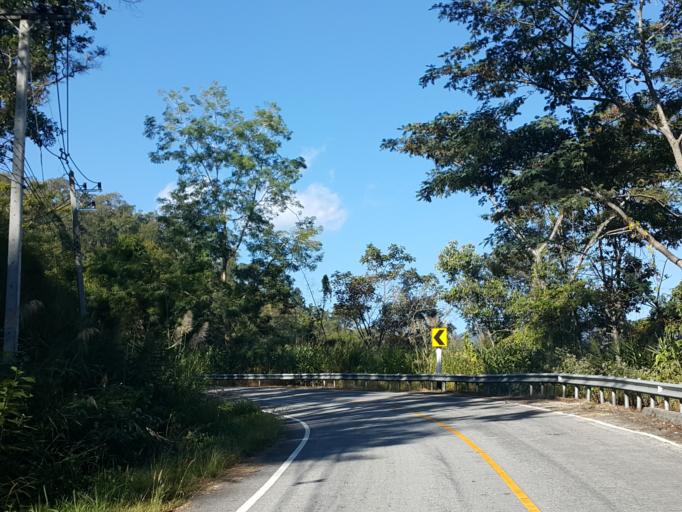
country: TH
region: Chiang Mai
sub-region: Amphoe Chiang Dao
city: Chiang Dao
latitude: 19.5275
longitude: 98.8812
